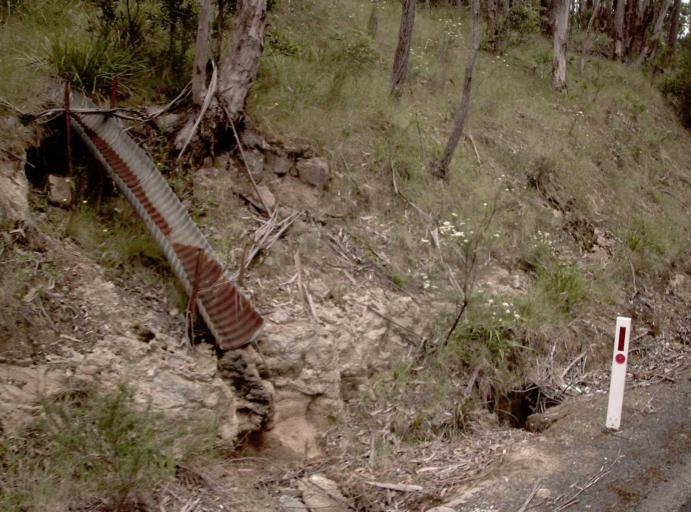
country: AU
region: New South Wales
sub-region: Bombala
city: Bombala
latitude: -37.2906
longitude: 149.2209
